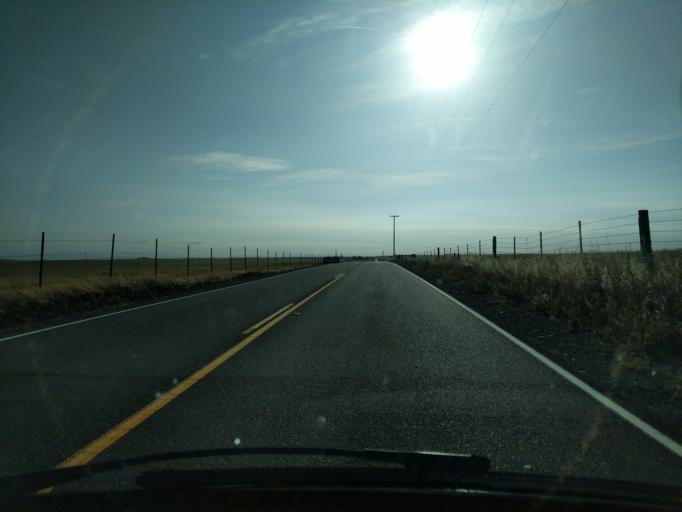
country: US
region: California
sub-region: San Joaquin County
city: Escalon
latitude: 37.9450
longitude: -120.9159
